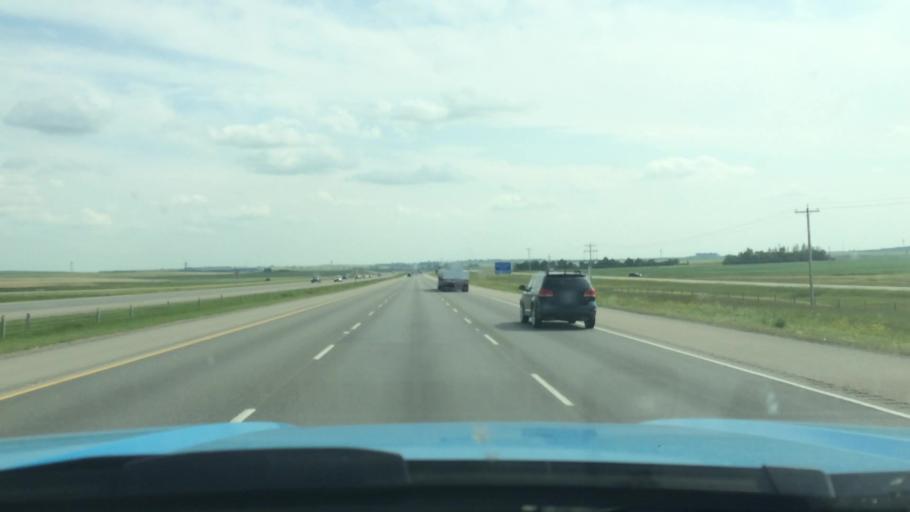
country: CA
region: Alberta
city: Crossfield
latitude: 51.4876
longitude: -114.0257
